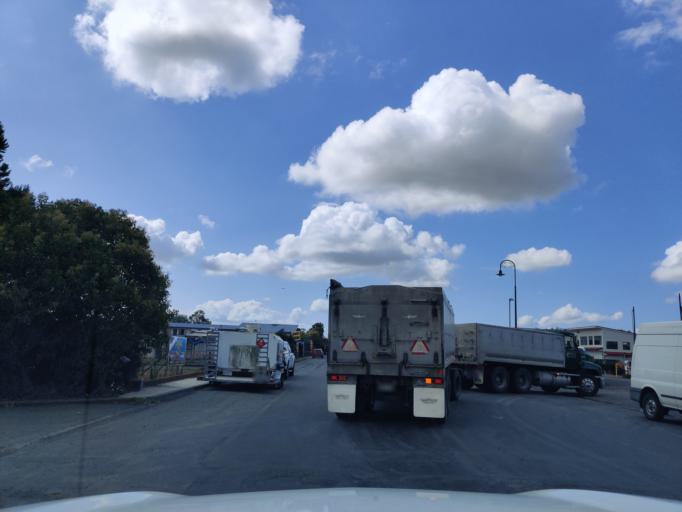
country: NZ
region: Auckland
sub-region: Auckland
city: Pukekohe East
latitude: -37.2460
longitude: 175.0226
